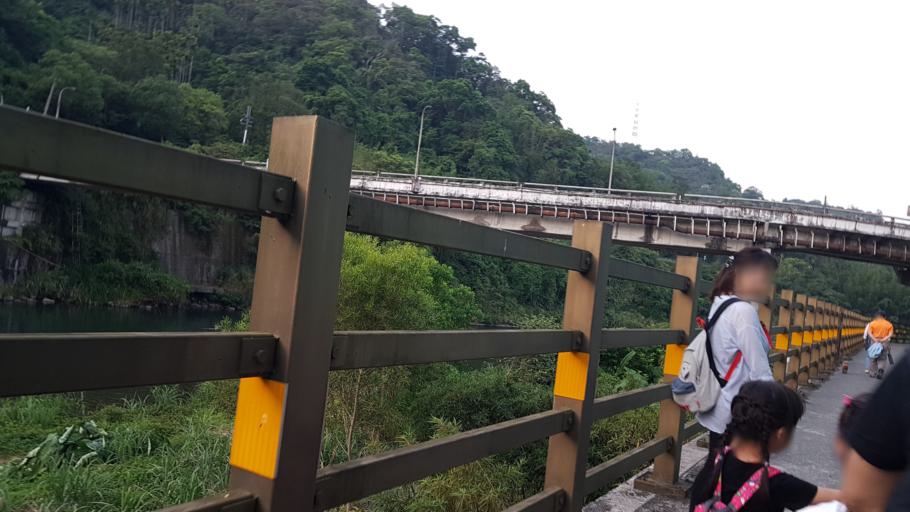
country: TW
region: Taiwan
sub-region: Yilan
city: Yilan
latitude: 24.9357
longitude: 121.7002
